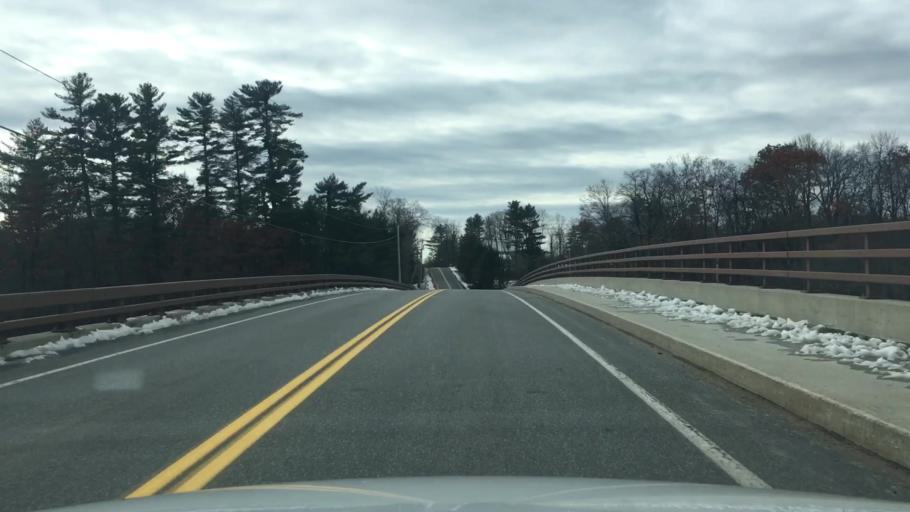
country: US
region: Maine
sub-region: Oxford County
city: Canton
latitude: 44.4612
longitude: -70.3041
